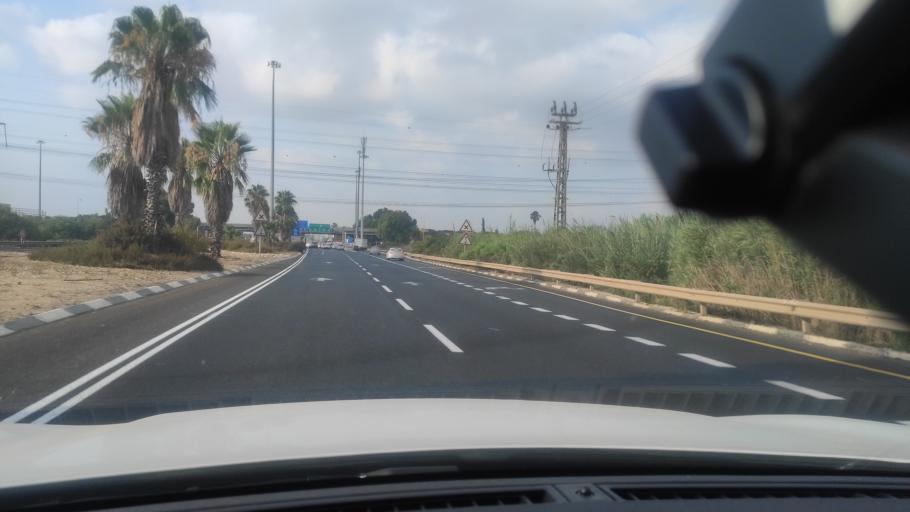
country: IL
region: Central District
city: Hod HaSharon
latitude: 32.1243
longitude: 34.9038
